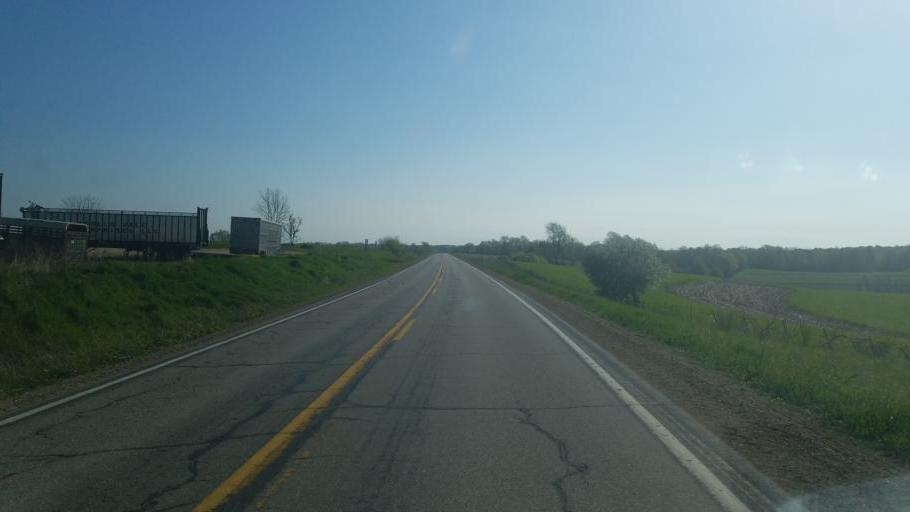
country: US
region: Wisconsin
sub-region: Vernon County
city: Hillsboro
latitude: 43.5957
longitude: -90.4808
